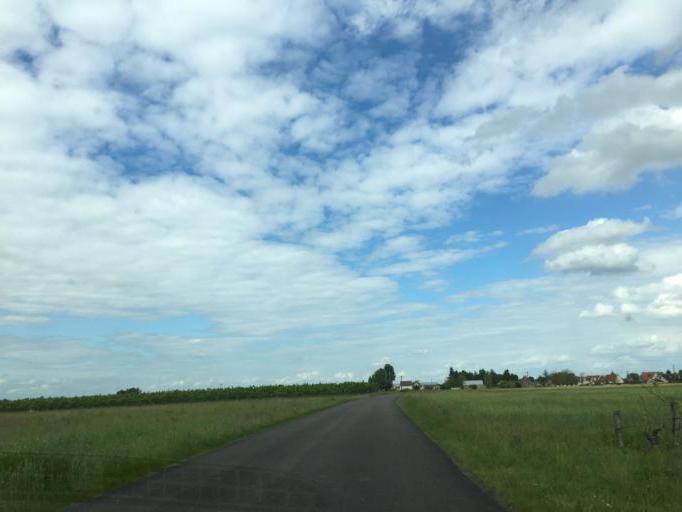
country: FR
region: Centre
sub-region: Departement du Loiret
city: Mareau-aux-Pres
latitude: 47.8304
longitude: 1.7923
